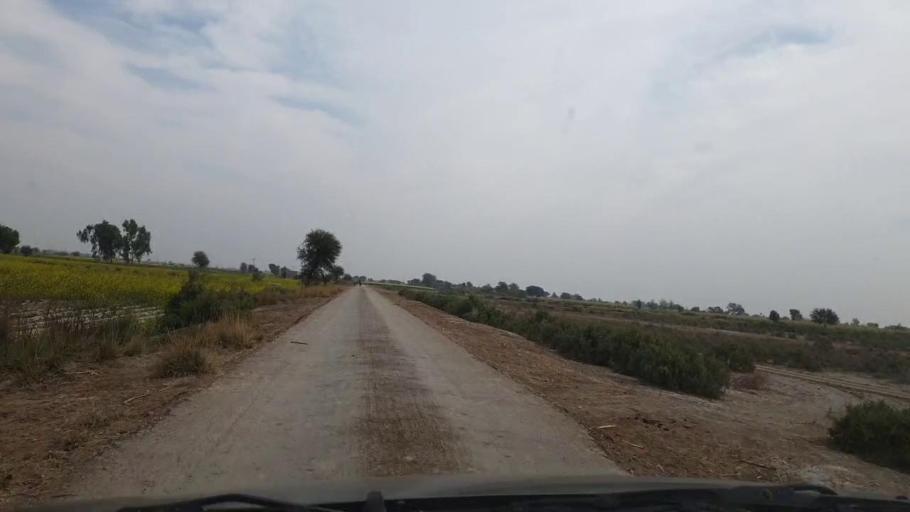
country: PK
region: Sindh
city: Sinjhoro
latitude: 26.0788
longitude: 68.8488
